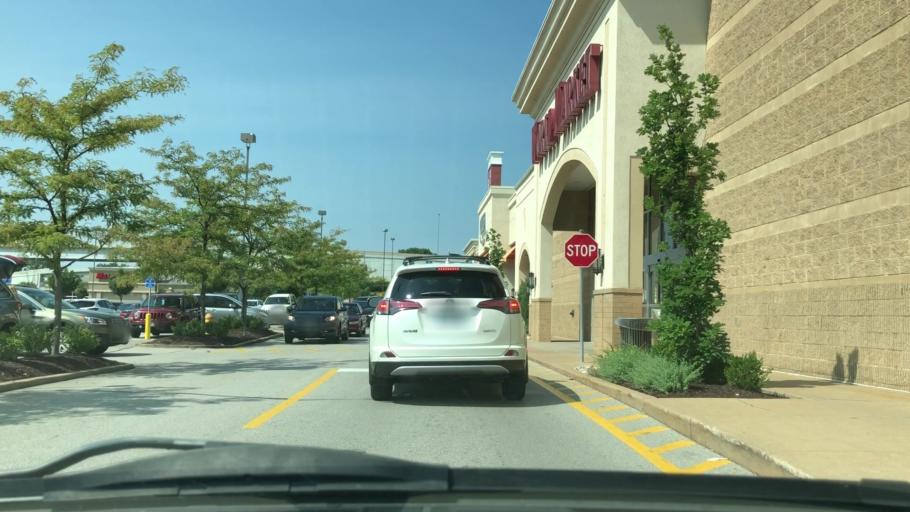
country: US
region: Missouri
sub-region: Saint Louis County
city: Brentwood
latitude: 38.6273
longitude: -90.3415
